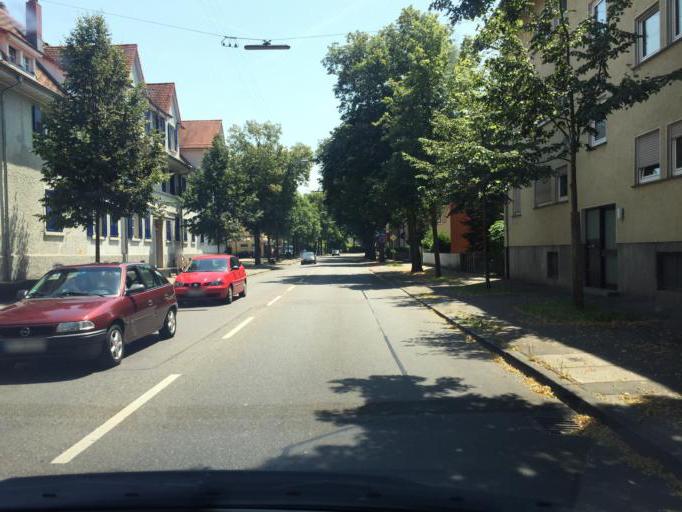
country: DE
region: Baden-Wuerttemberg
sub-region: Freiburg Region
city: Singen
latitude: 47.7541
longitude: 8.8401
